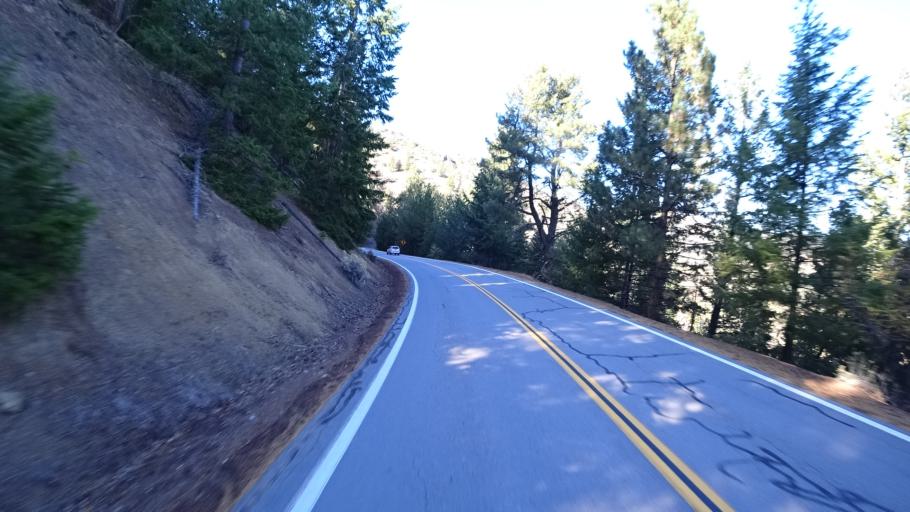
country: US
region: California
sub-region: Siskiyou County
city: Weed
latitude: 41.4432
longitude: -122.6438
